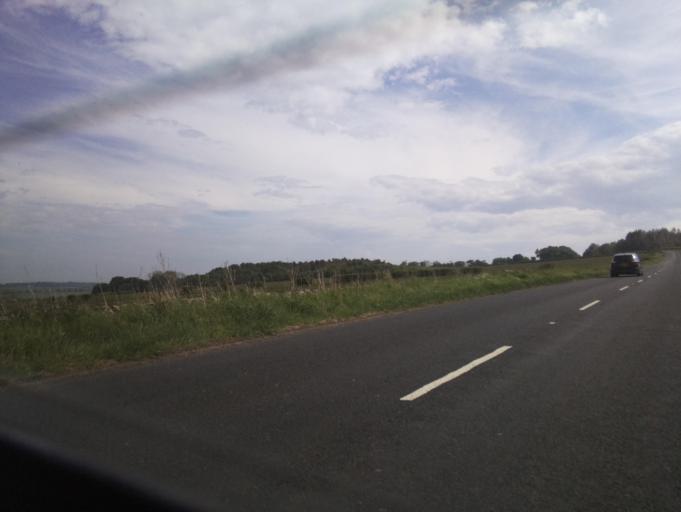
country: GB
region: England
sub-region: Northumberland
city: Alnwick
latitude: 55.4445
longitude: -1.7102
